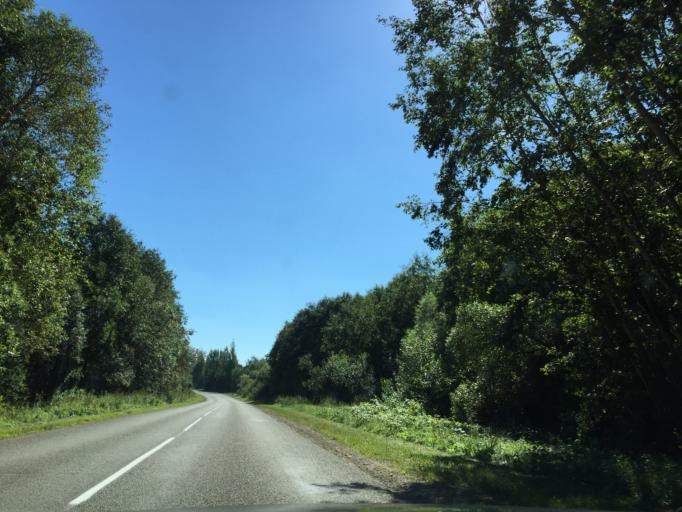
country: LV
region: Akniste
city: Akniste
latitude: 56.1239
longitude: 25.8310
